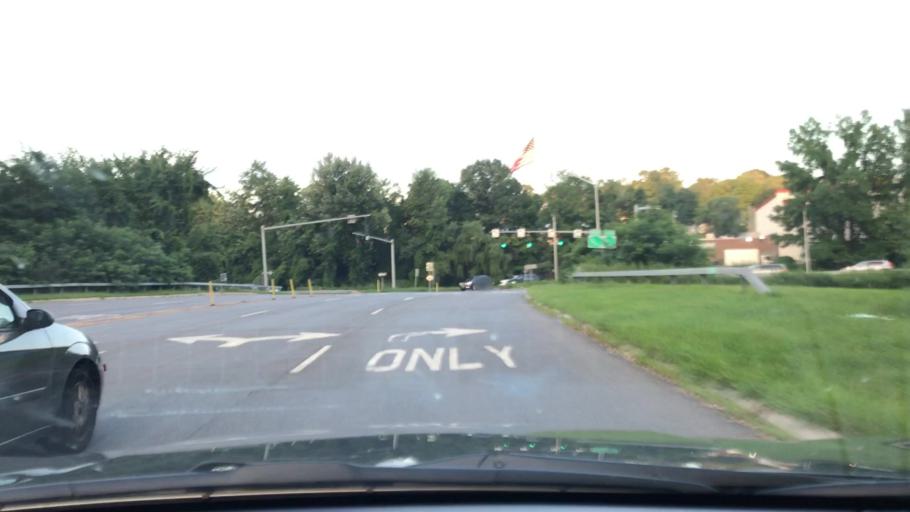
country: US
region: New York
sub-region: Westchester County
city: Hastings-on-Hudson
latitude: 40.9698
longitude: -73.8714
